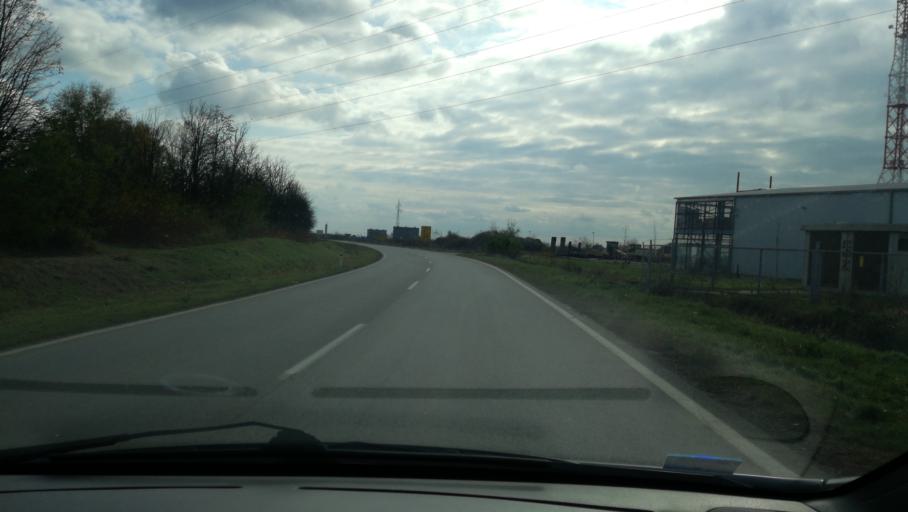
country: RS
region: Autonomna Pokrajina Vojvodina
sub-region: Severnobanatski Okrug
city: Kikinda
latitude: 45.8093
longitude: 20.4325
